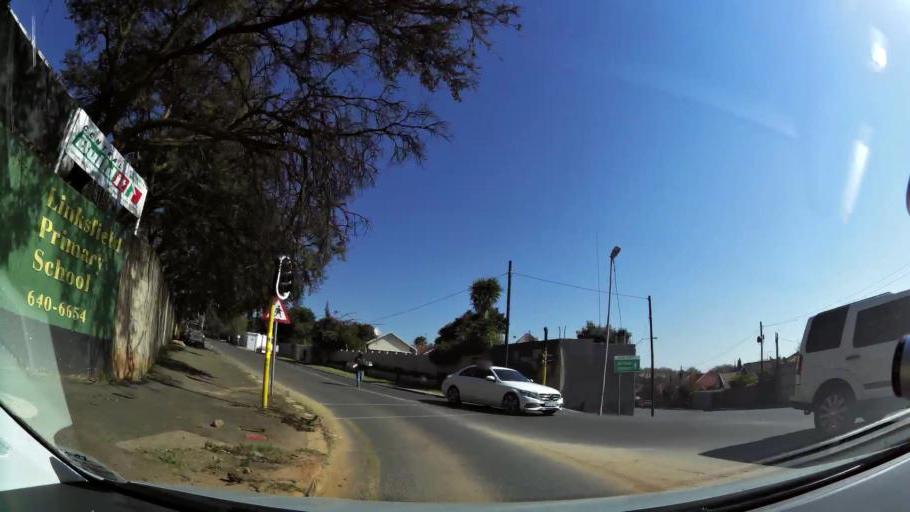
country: ZA
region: Gauteng
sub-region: City of Johannesburg Metropolitan Municipality
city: Johannesburg
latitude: -26.1644
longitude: 28.0913
